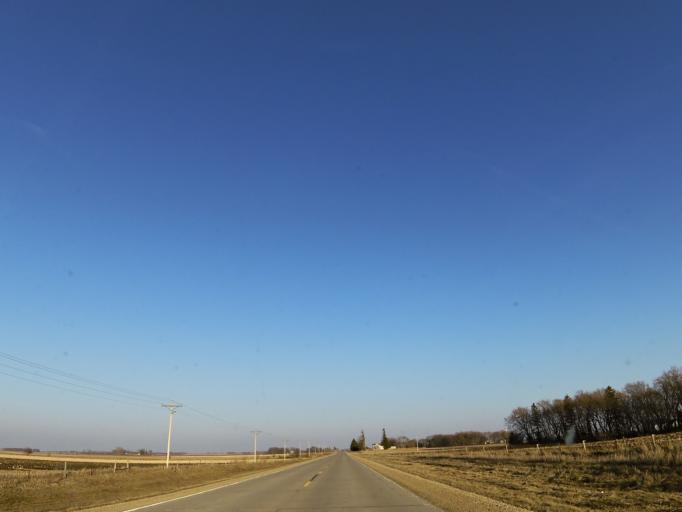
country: US
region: Iowa
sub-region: Worth County
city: Northwood
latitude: 43.4382
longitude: -93.1082
